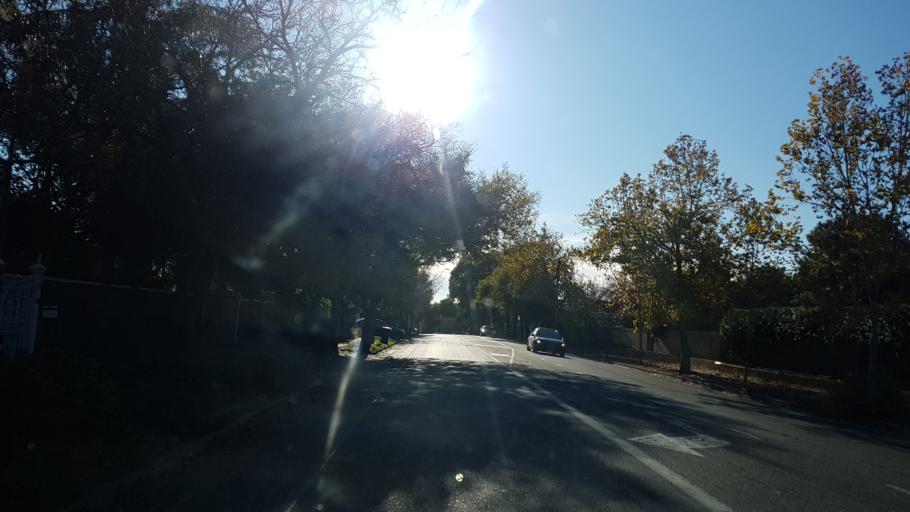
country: AU
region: South Australia
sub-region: Norwood Payneham St Peters
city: Royston Park
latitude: -34.9058
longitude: 138.6246
